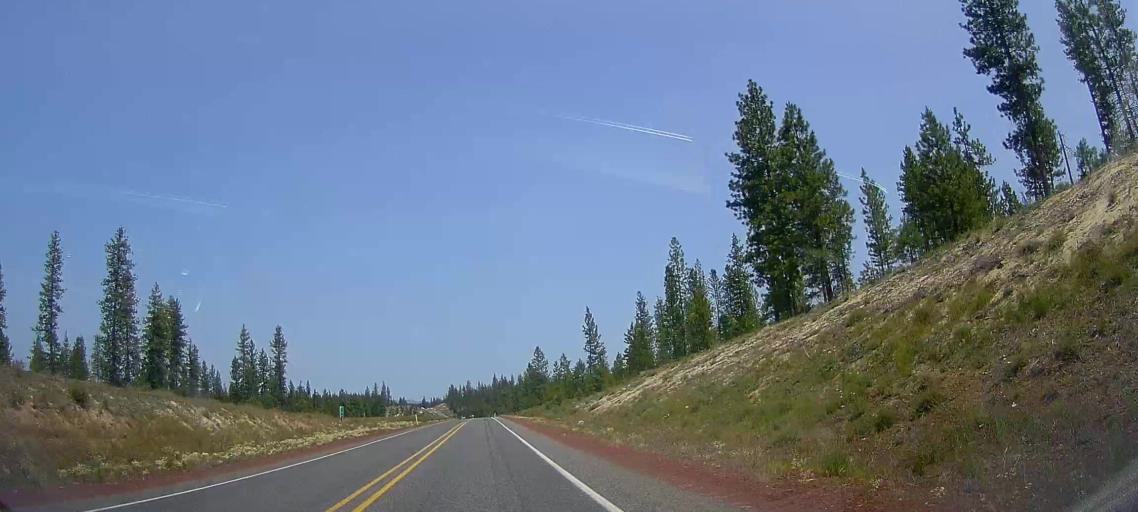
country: US
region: Oregon
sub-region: Deschutes County
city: La Pine
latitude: 43.4157
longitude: -121.7194
